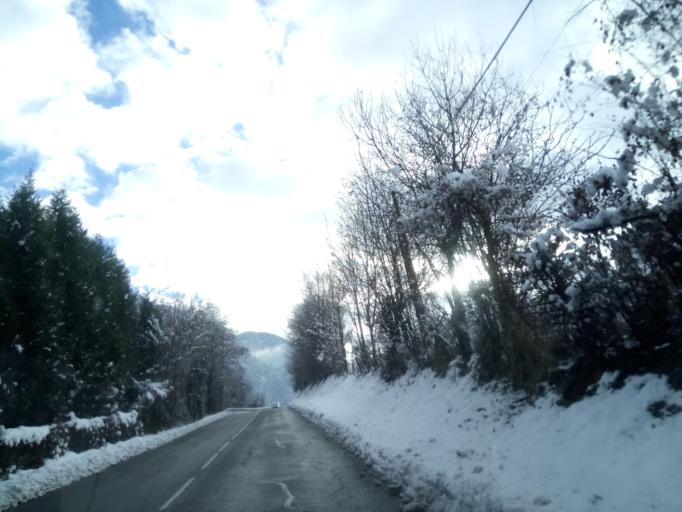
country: FR
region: Rhone-Alpes
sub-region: Departement de la Savoie
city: Saint-Jean-de-Maurienne
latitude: 45.2709
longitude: 6.3364
